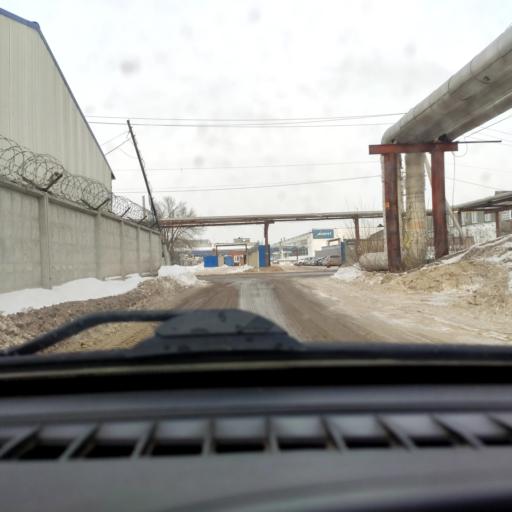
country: RU
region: Samara
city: Tol'yatti
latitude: 53.5752
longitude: 49.2817
